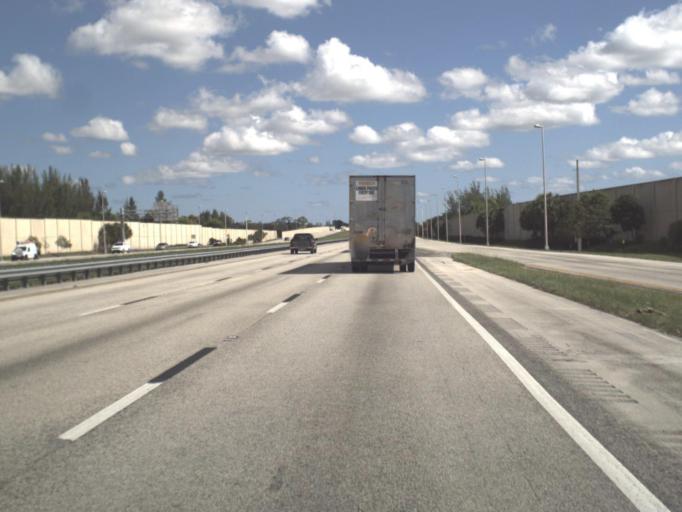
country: US
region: Florida
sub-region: Broward County
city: Parkland
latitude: 26.3016
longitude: -80.2454
